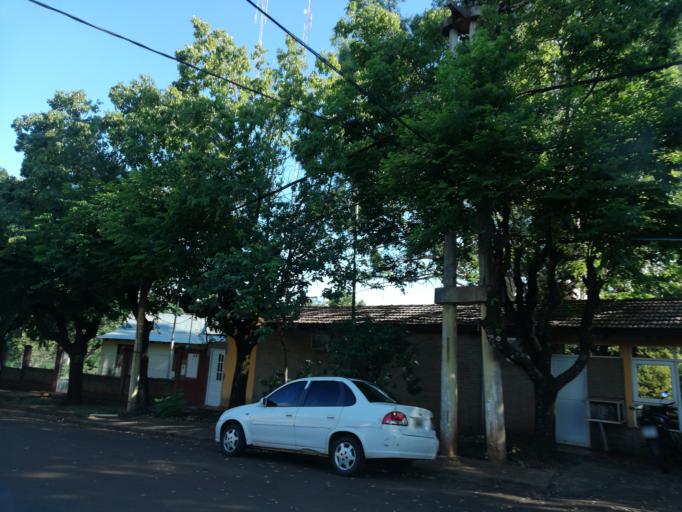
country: AR
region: Misiones
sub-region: Departamento de Capital
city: Posadas
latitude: -27.4033
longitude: -55.9256
